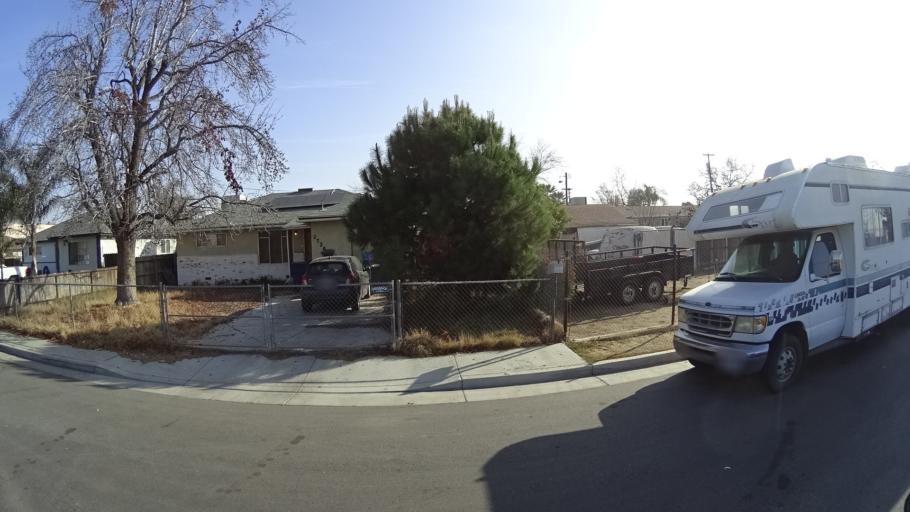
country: US
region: California
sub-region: Kern County
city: Bakersfield
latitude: 35.3294
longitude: -119.0234
